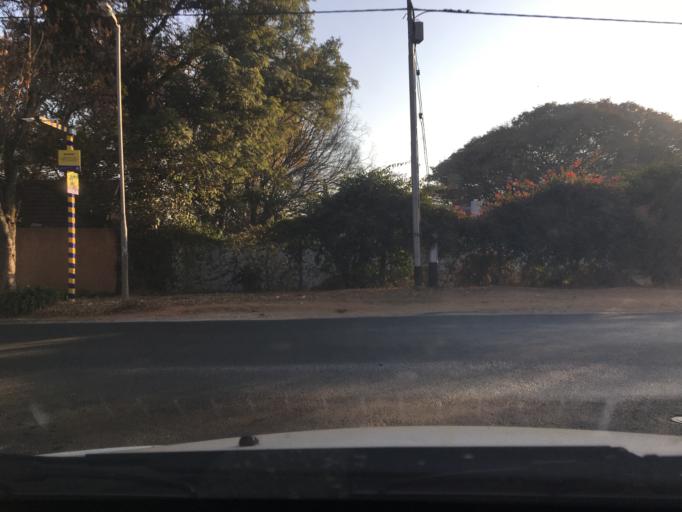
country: ZA
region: Gauteng
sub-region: City of Johannesburg Metropolitan Municipality
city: Johannesburg
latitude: -26.0709
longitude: 28.0177
